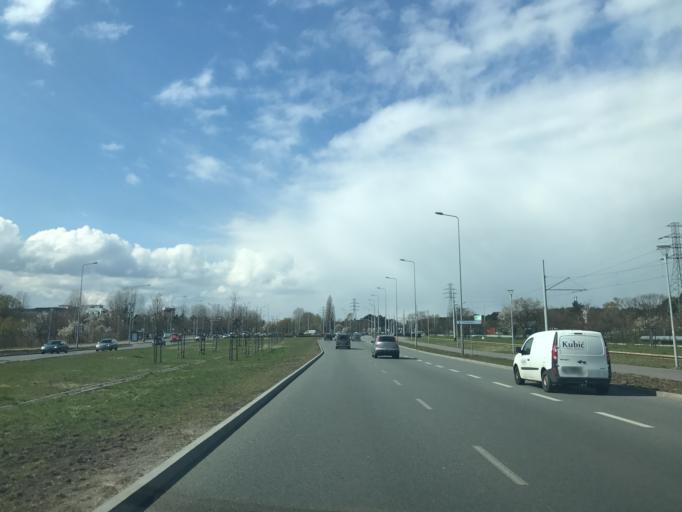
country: PL
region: Pomeranian Voivodeship
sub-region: Gdansk
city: Gdansk
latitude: 54.4003
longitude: 18.6259
